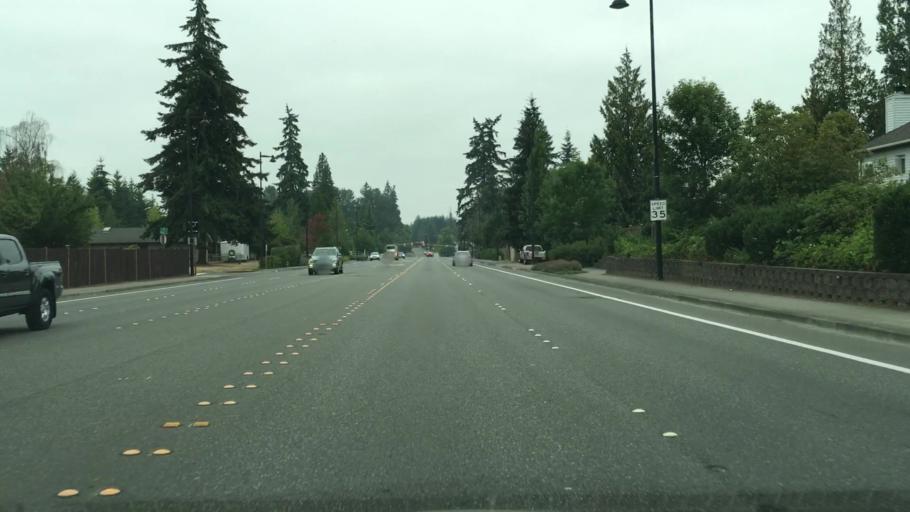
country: US
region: Washington
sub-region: King County
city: Newcastle
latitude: 47.5092
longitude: -122.1562
